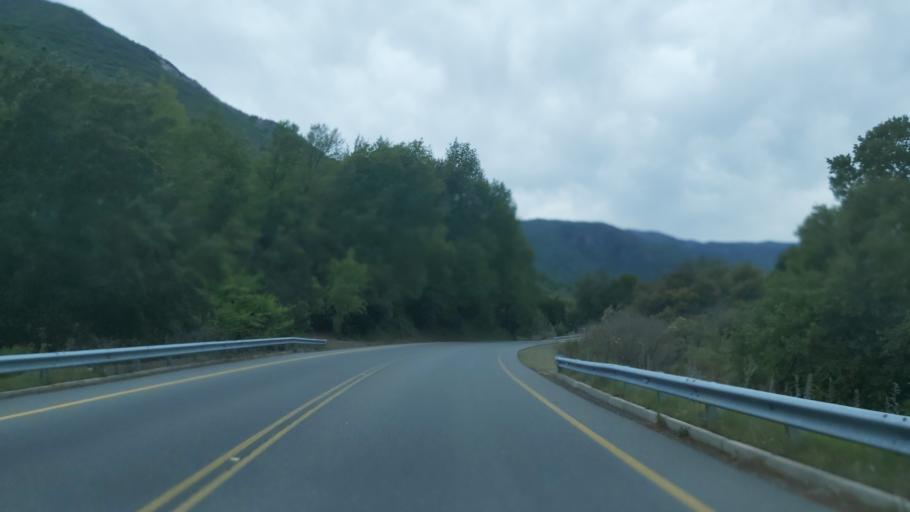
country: CL
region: Maule
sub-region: Provincia de Linares
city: Colbun
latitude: -35.7142
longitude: -71.0453
